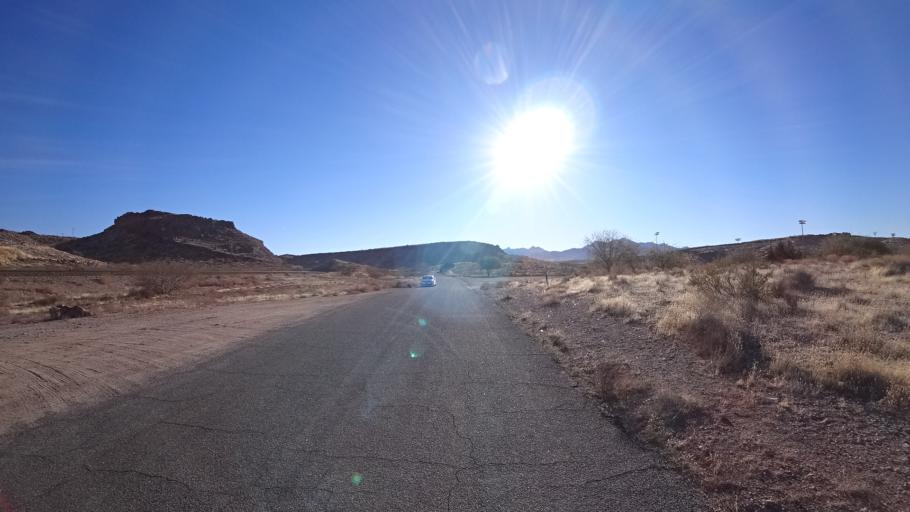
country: US
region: Arizona
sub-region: Mohave County
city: Kingman
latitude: 35.1846
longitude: -114.0388
